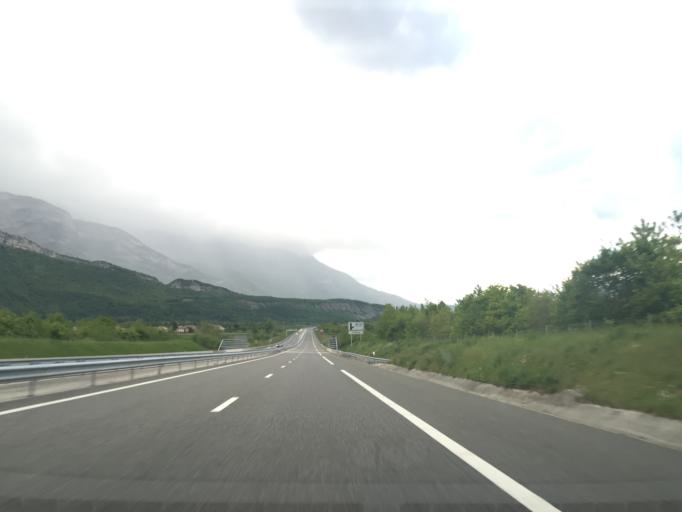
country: FR
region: Rhone-Alpes
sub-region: Departement de l'Isere
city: Vif
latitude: 45.0567
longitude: 5.6859
